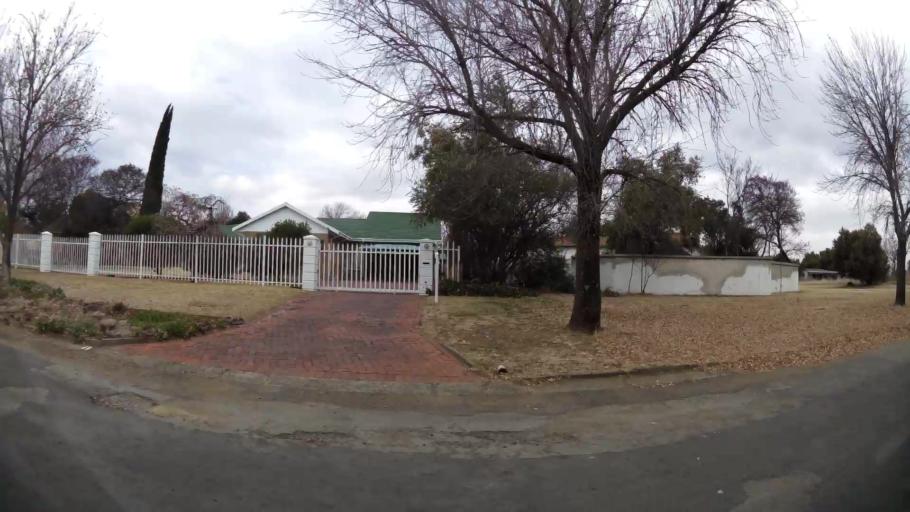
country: ZA
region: Orange Free State
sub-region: Fezile Dabi District Municipality
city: Kroonstad
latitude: -27.6863
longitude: 27.2365
